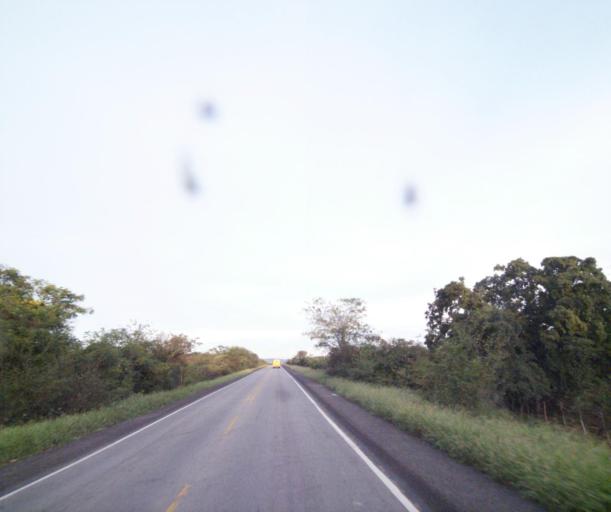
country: BR
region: Bahia
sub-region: Brumado
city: Brumado
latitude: -14.2574
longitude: -41.7740
